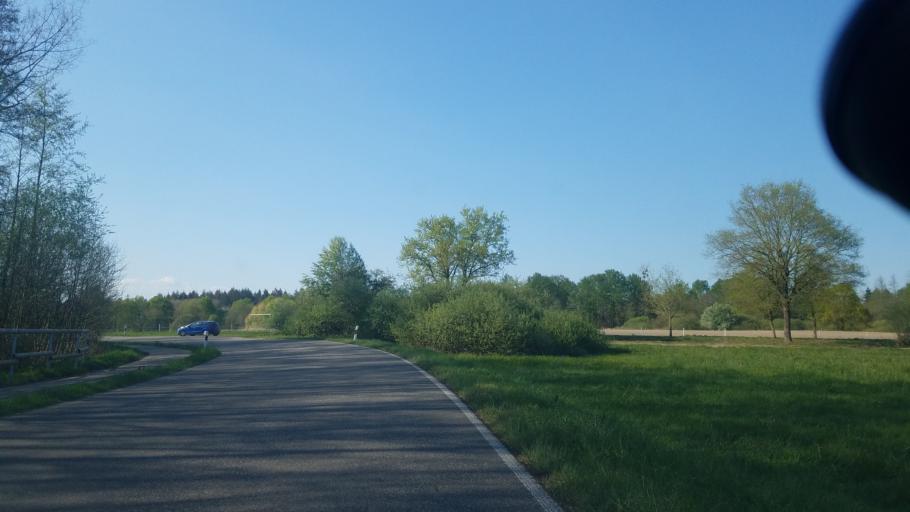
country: DE
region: Baden-Wuerttemberg
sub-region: Karlsruhe Region
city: Hugelsheim
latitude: 48.7692
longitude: 8.1111
